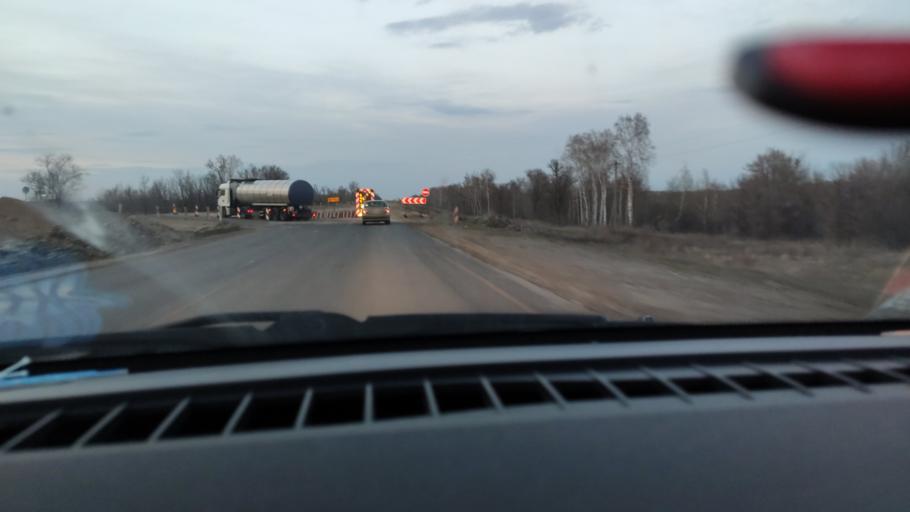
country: RU
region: Saratov
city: Sinodskoye
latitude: 52.0208
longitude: 46.7060
